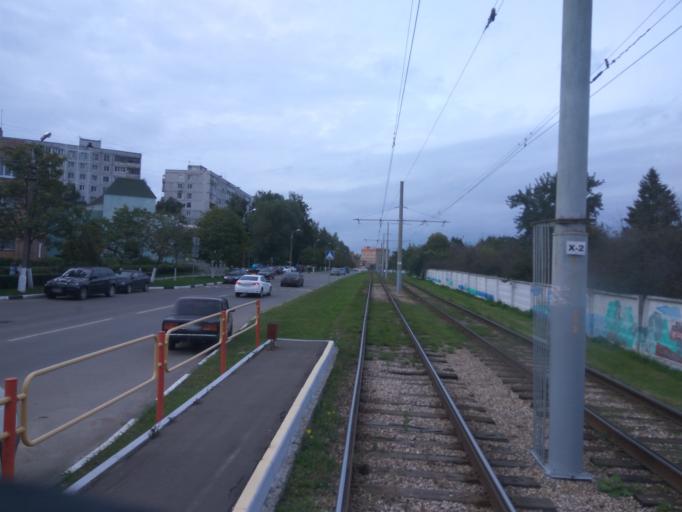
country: RU
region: Moskovskaya
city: Kolomna
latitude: 55.0612
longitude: 38.7576
